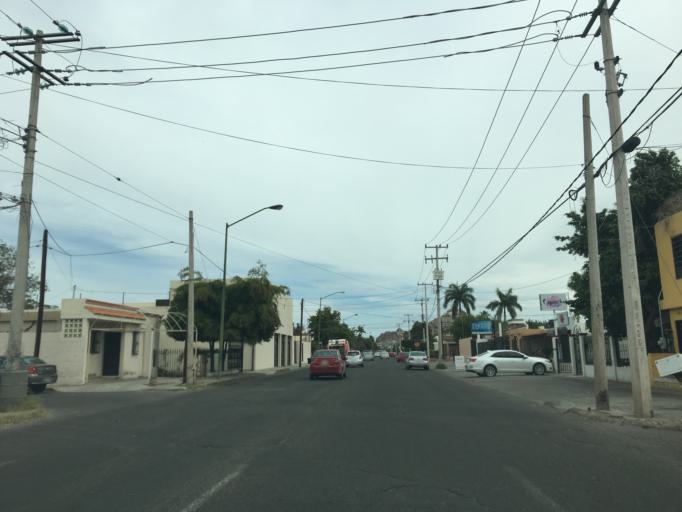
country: MX
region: Sonora
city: Hermosillo
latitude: 29.0735
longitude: -110.9713
